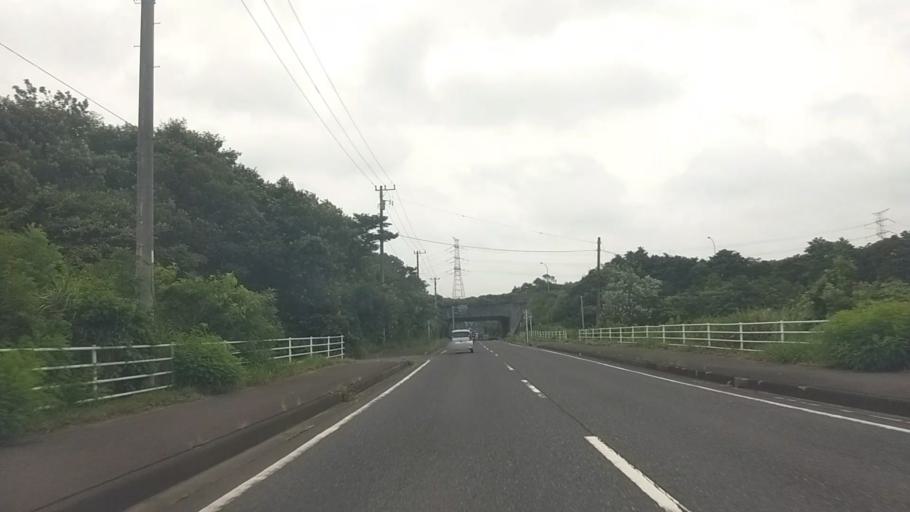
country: JP
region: Chiba
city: Kisarazu
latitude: 35.3873
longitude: 139.9965
